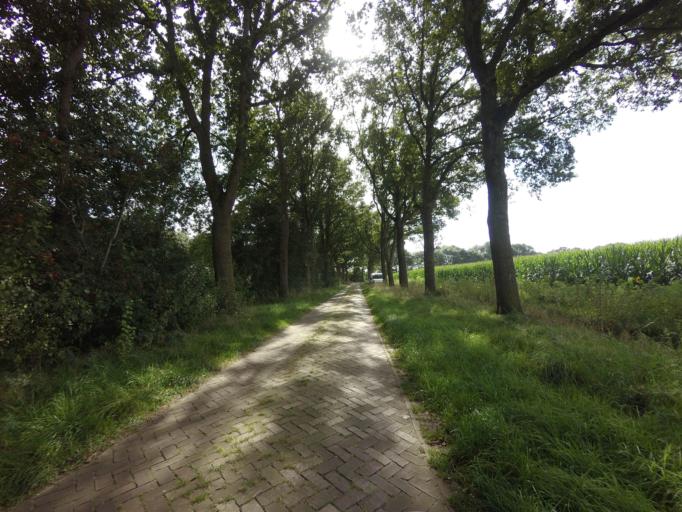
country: NL
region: Drenthe
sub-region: Gemeente Coevorden
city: Sleen
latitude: 52.7769
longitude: 6.7237
